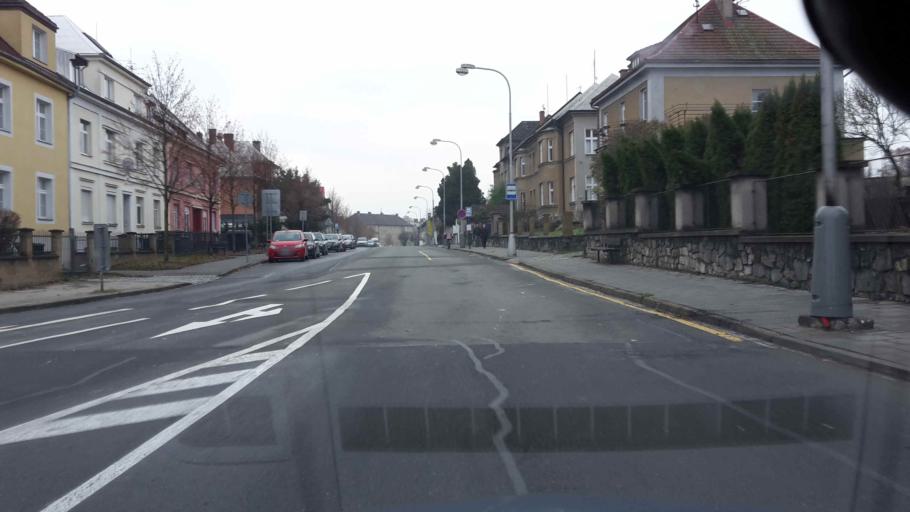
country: CZ
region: Olomoucky
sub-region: Okres Olomouc
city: Olomouc
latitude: 49.6016
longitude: 17.2367
